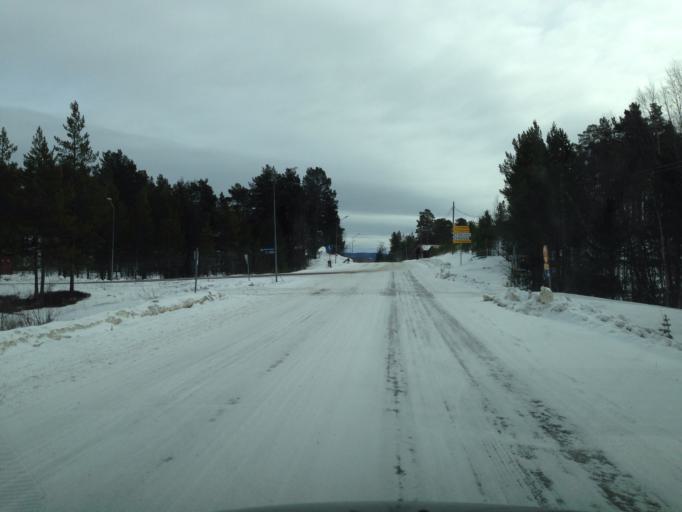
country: SE
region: Jaemtland
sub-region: Harjedalens Kommun
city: Sveg
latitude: 62.1134
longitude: 13.2616
